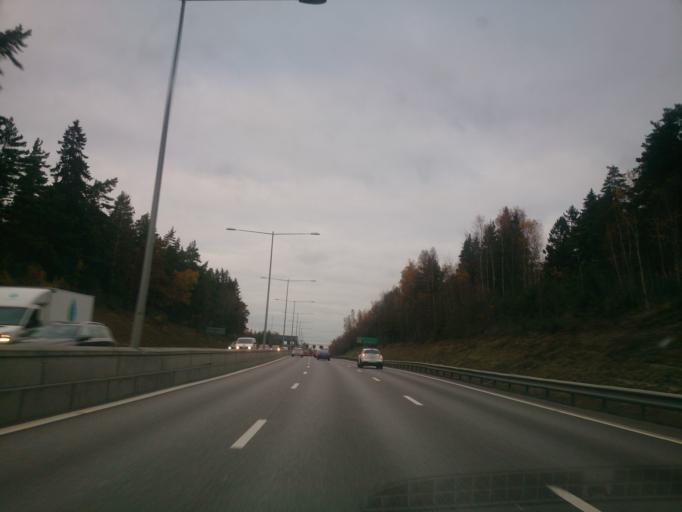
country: SE
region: Stockholm
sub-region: Botkyrka Kommun
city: Eriksberg
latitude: 59.2194
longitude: 17.7826
